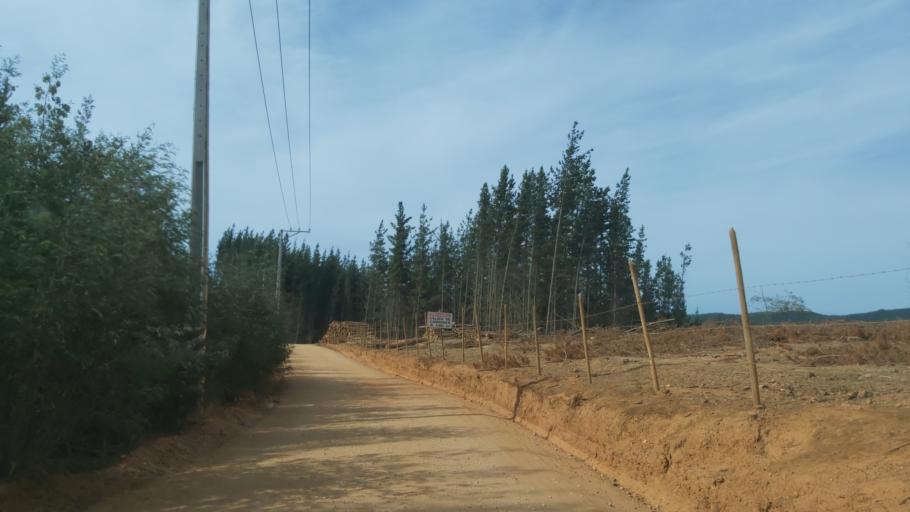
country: CL
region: Maule
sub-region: Provincia de Talca
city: Constitucion
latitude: -34.8517
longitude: -72.0334
